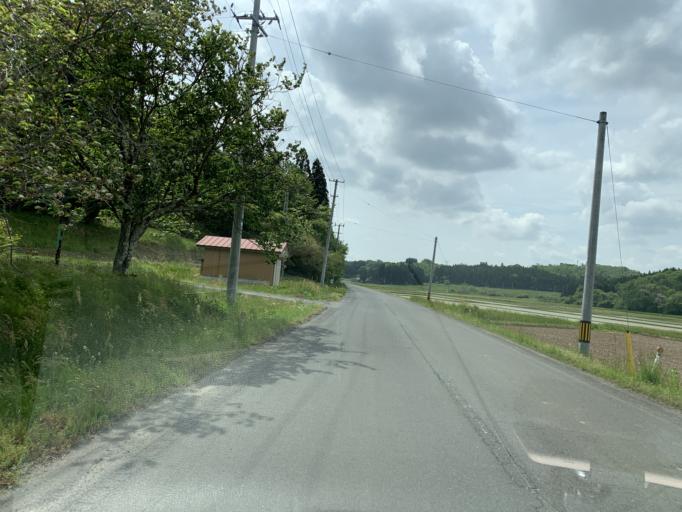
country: JP
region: Iwate
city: Ichinoseki
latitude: 38.8559
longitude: 141.0051
